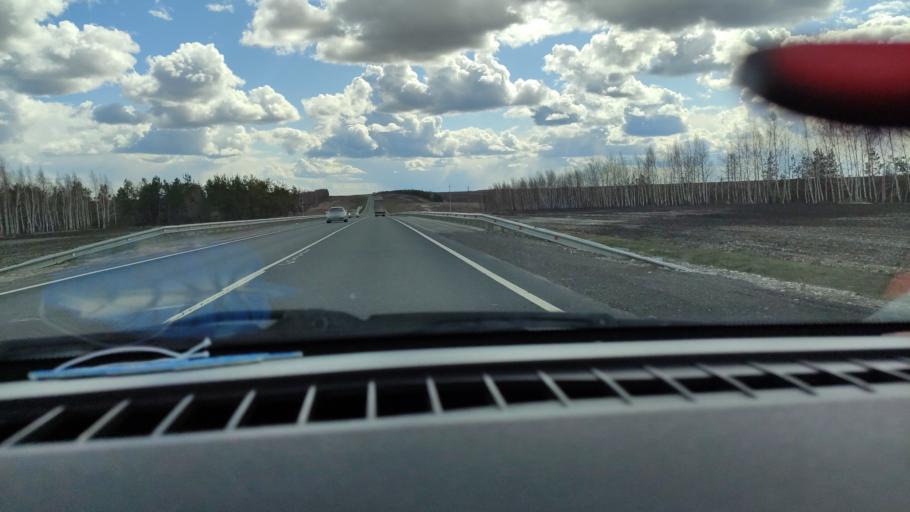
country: RU
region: Samara
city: Syzran'
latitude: 52.8993
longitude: 48.2960
